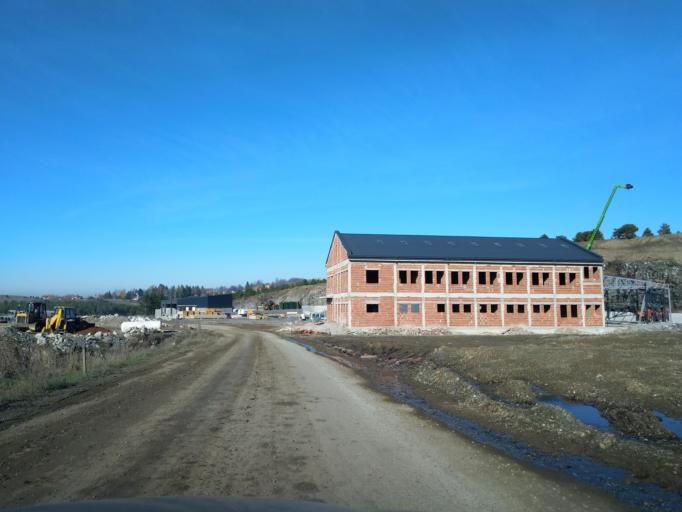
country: RS
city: Zlatibor
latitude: 43.7297
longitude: 19.6821
